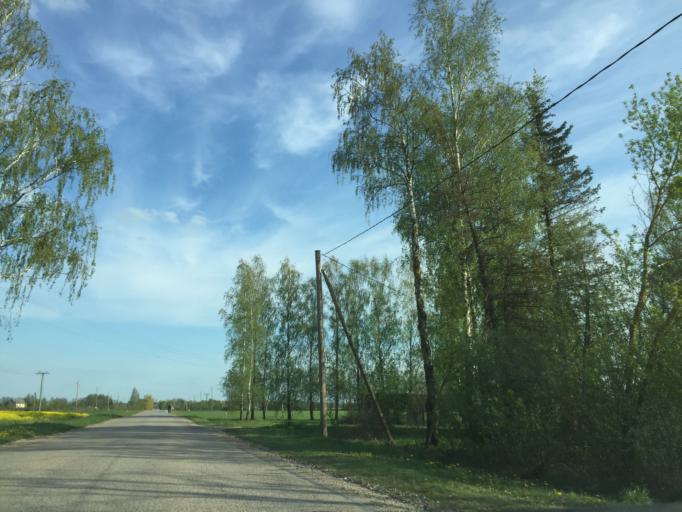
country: LV
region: Bauskas Rajons
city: Bauska
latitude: 56.3354
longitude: 24.2418
